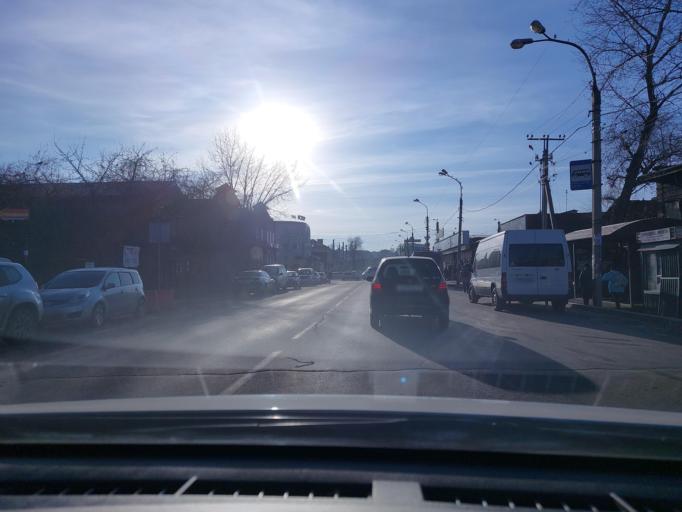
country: RU
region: Irkutsk
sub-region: Irkutskiy Rayon
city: Irkutsk
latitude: 52.2816
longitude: 104.3007
